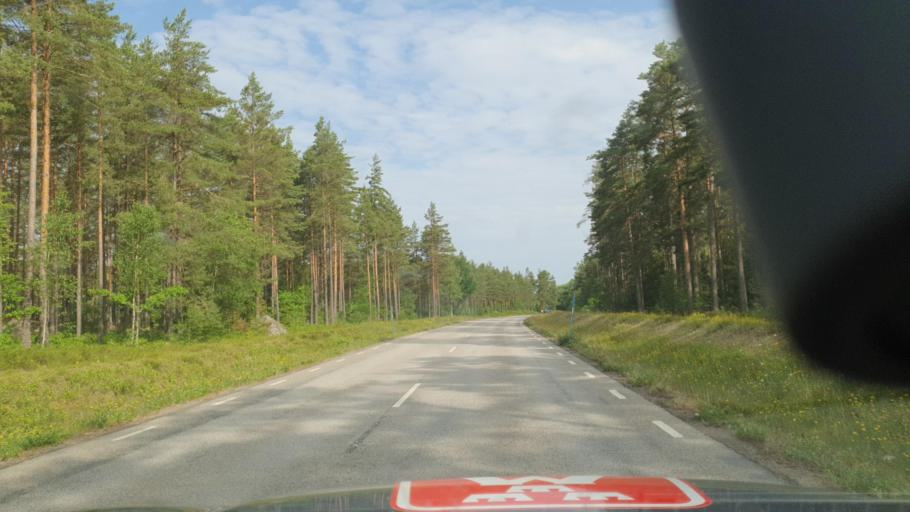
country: SE
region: Kalmar
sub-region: Nybro Kommun
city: Nybro
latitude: 56.6879
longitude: 15.9868
